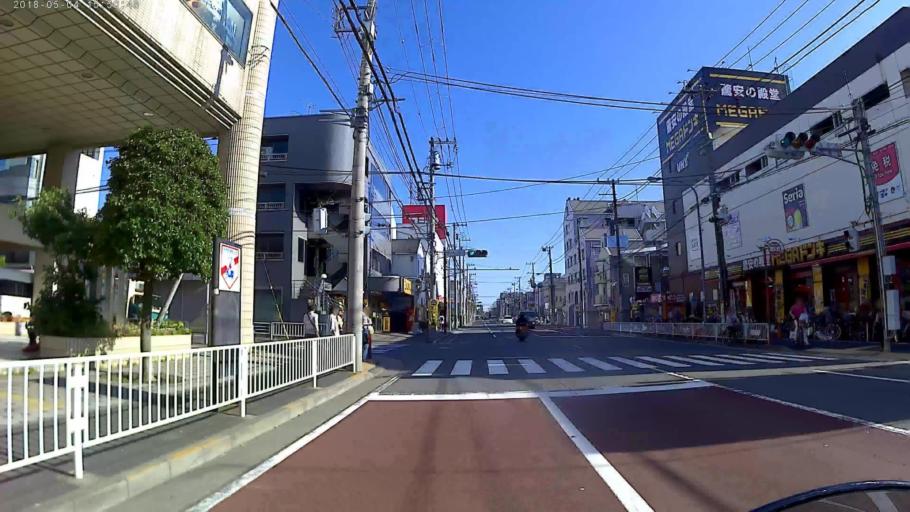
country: JP
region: Kanagawa
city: Yokohama
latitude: 35.4939
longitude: 139.6480
